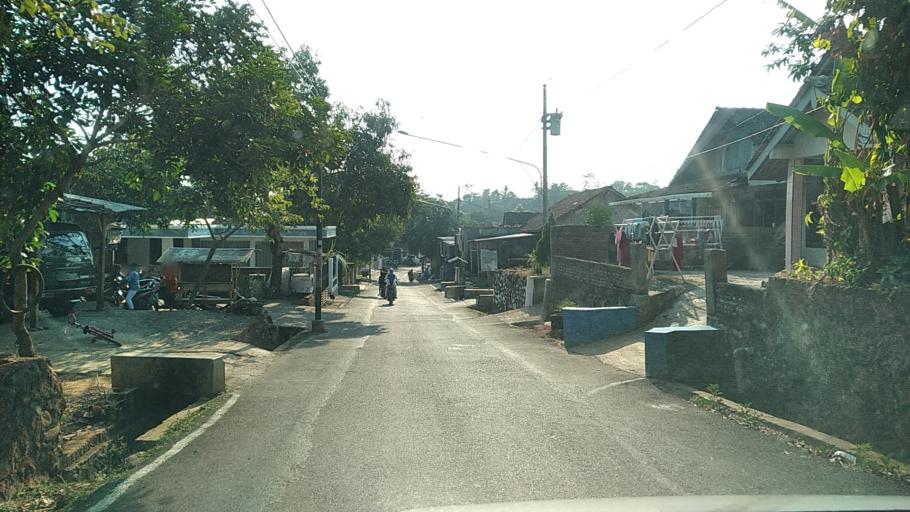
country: ID
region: Central Java
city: Semarang
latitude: -7.0384
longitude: 110.2939
